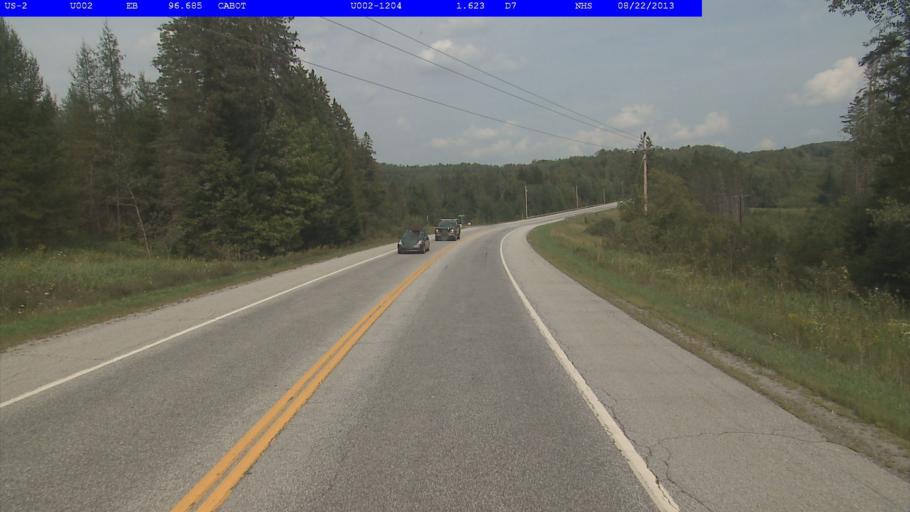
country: US
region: Vermont
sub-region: Caledonia County
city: Hardwick
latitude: 44.3663
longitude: -72.2937
